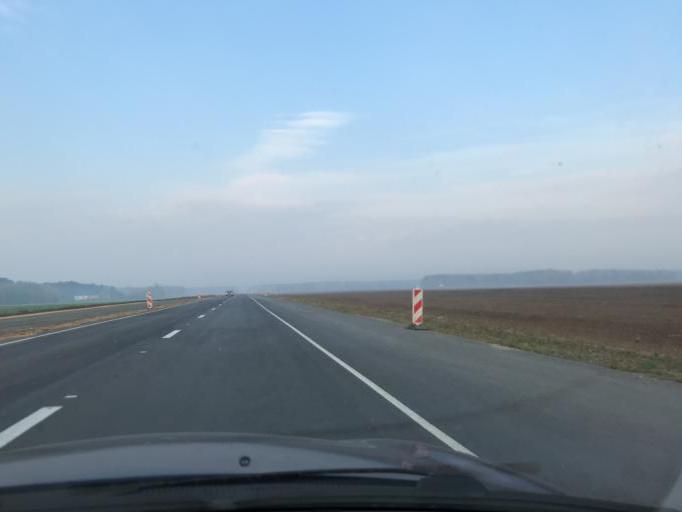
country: BY
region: Grodnenskaya
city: Lida
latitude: 53.8381
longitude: 25.2797
